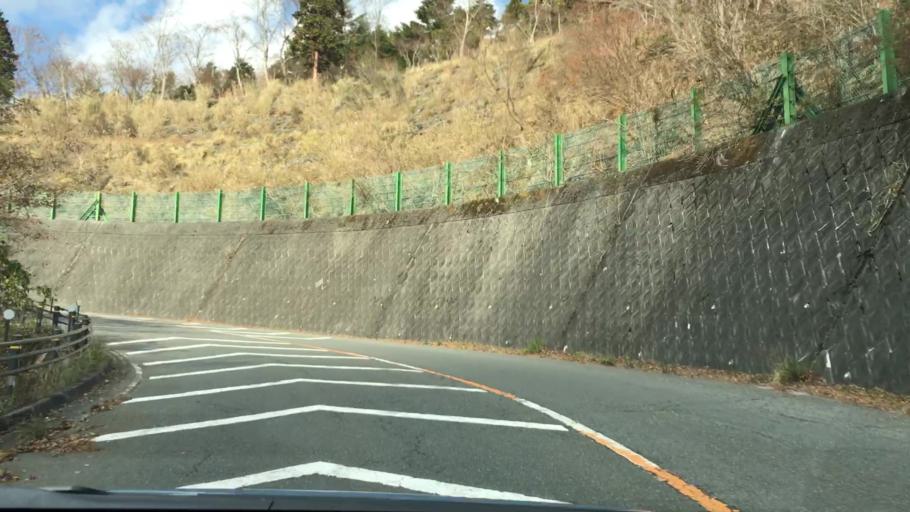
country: JP
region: Shizuoka
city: Gotemba
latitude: 35.3993
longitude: 138.9412
